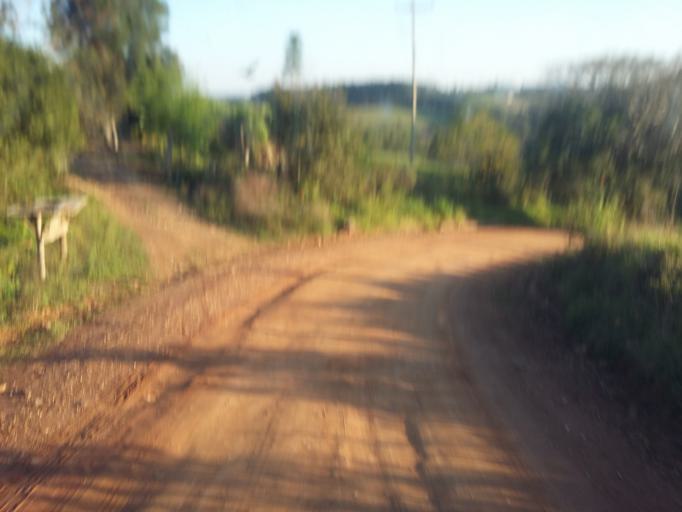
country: BR
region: Rio Grande do Sul
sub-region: Camaqua
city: Camaqua
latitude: -30.7203
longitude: -51.7705
